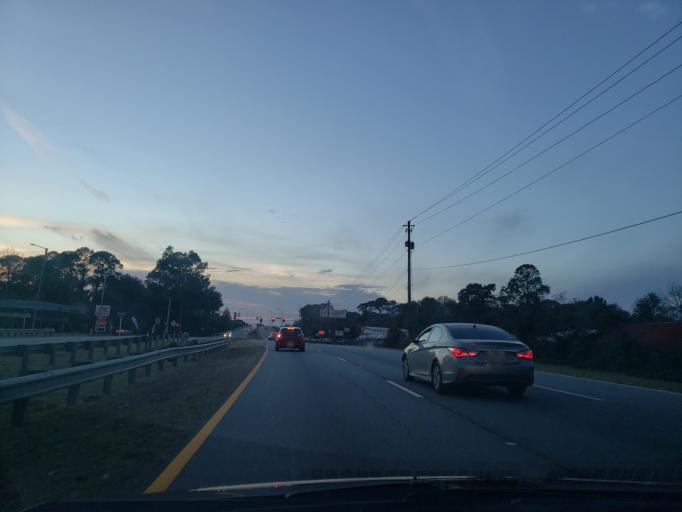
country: US
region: Georgia
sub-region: Dougherty County
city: Albany
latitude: 31.5725
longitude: -84.1161
